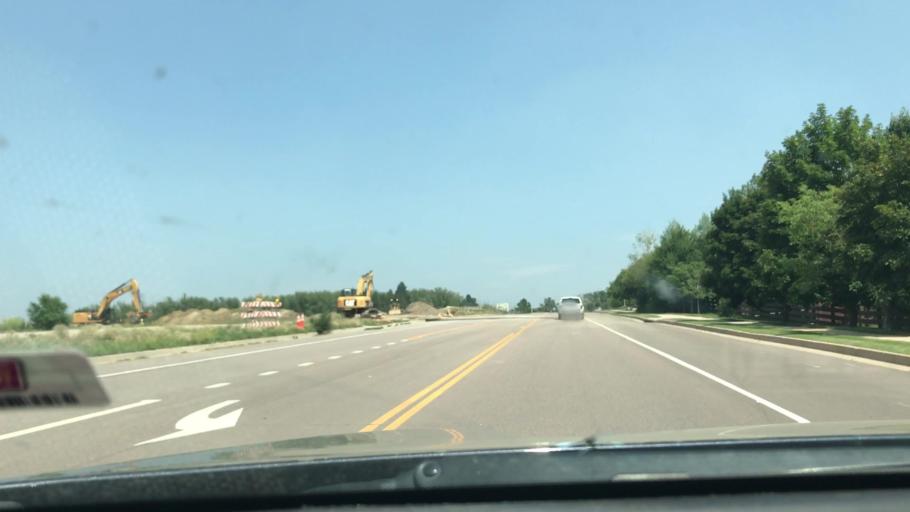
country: US
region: Colorado
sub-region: El Paso County
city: Gleneagle
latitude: 38.9819
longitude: -104.7781
